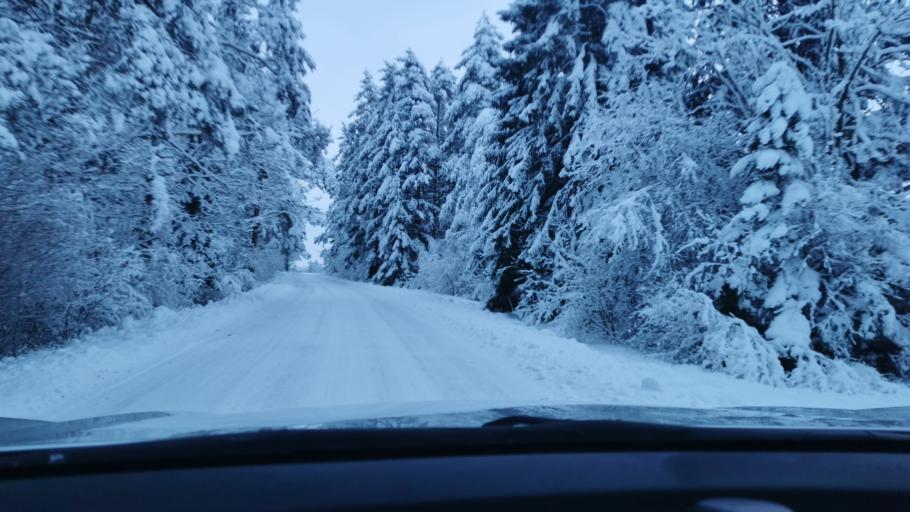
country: EE
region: Laeaene-Virumaa
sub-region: Haljala vald
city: Haljala
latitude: 59.4961
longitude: 26.3098
